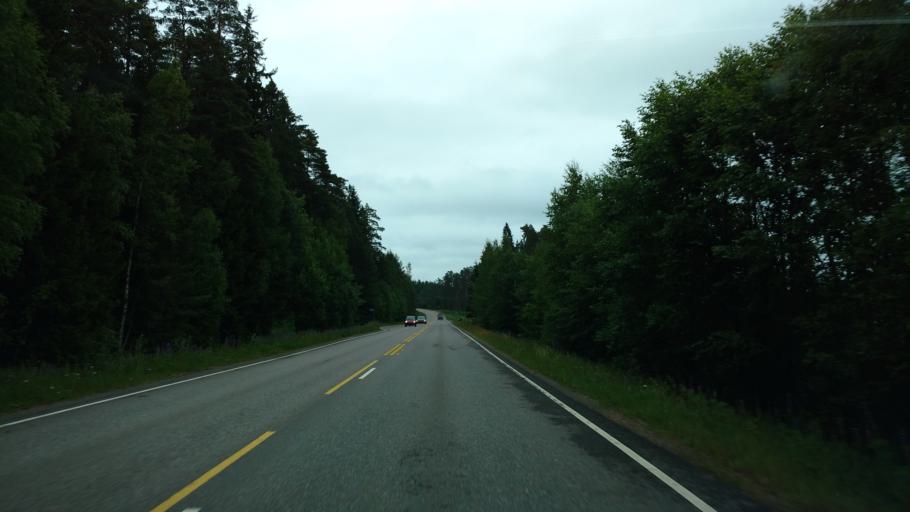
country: FI
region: Varsinais-Suomi
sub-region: Salo
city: Kiikala
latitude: 60.4194
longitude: 23.5879
